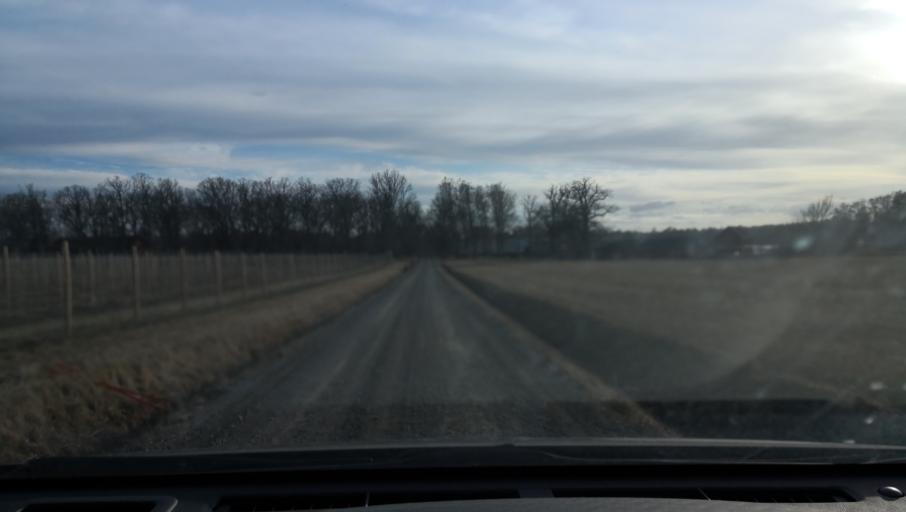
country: SE
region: Uppsala
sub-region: Enkopings Kommun
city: Dalby
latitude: 59.4774
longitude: 17.2532
